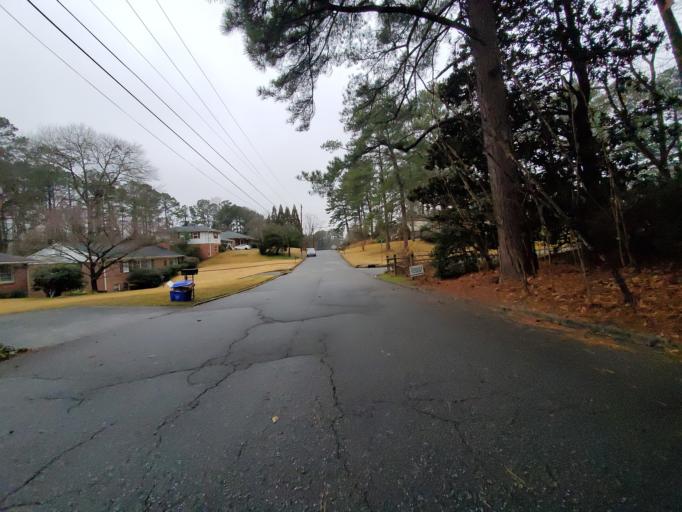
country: US
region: Georgia
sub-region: DeKalb County
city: North Decatur
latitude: 33.7987
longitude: -84.3030
